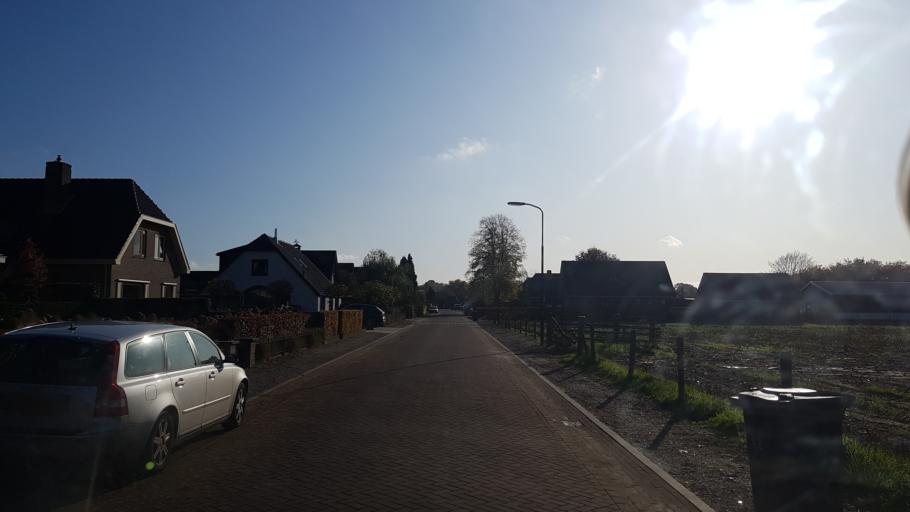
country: NL
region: Gelderland
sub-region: Gemeente Apeldoorn
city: Uddel
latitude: 52.2619
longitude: 5.7799
